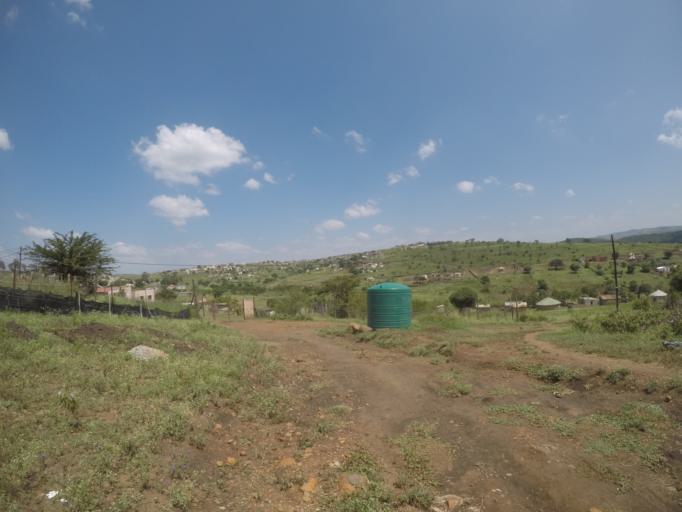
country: ZA
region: KwaZulu-Natal
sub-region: uThungulu District Municipality
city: Empangeni
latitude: -28.6002
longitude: 31.7389
